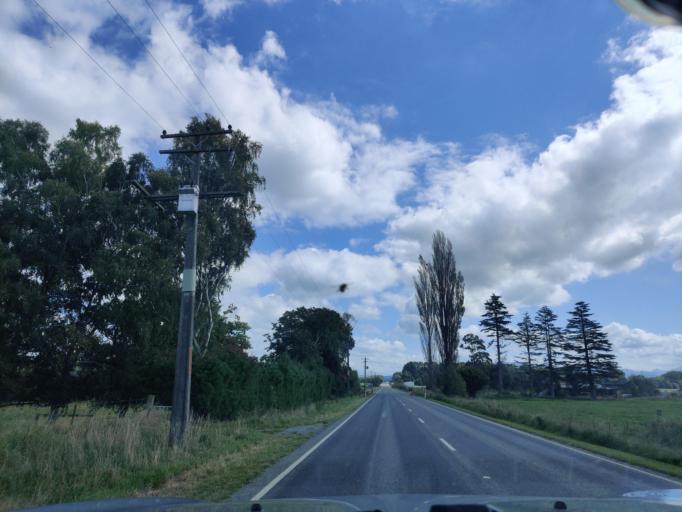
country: NZ
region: Canterbury
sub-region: Timaru District
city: Pleasant Point
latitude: -44.1265
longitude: 171.2675
